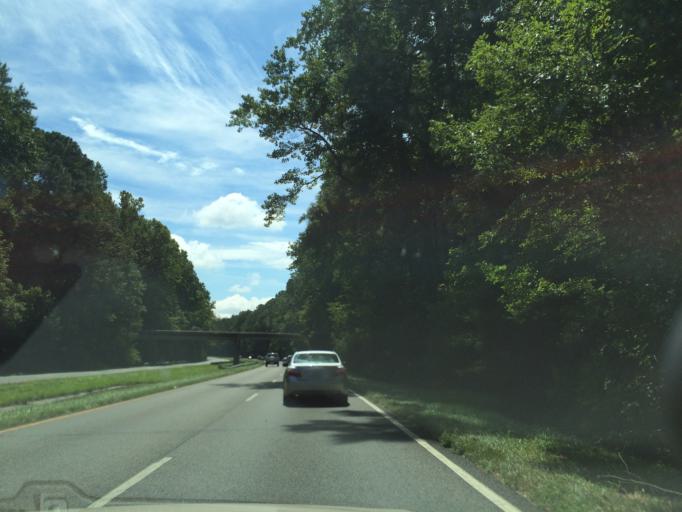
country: US
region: Virginia
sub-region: York County
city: Yorktown
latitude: 37.2167
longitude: -76.5153
